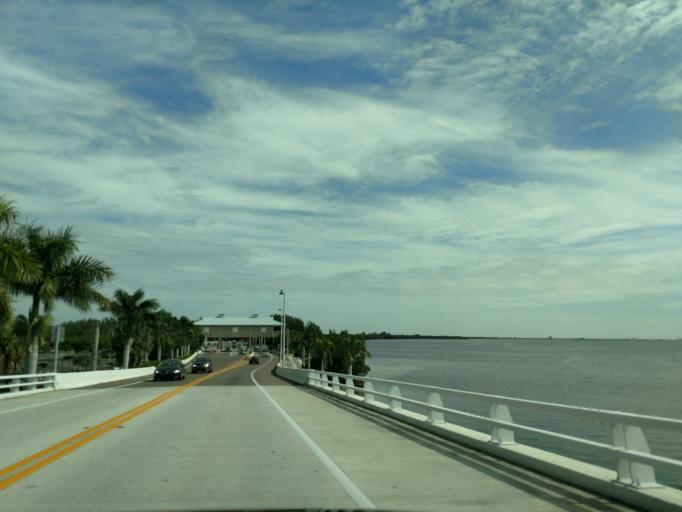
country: US
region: Florida
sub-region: Lee County
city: Punta Rassa
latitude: 26.4840
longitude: -82.0106
